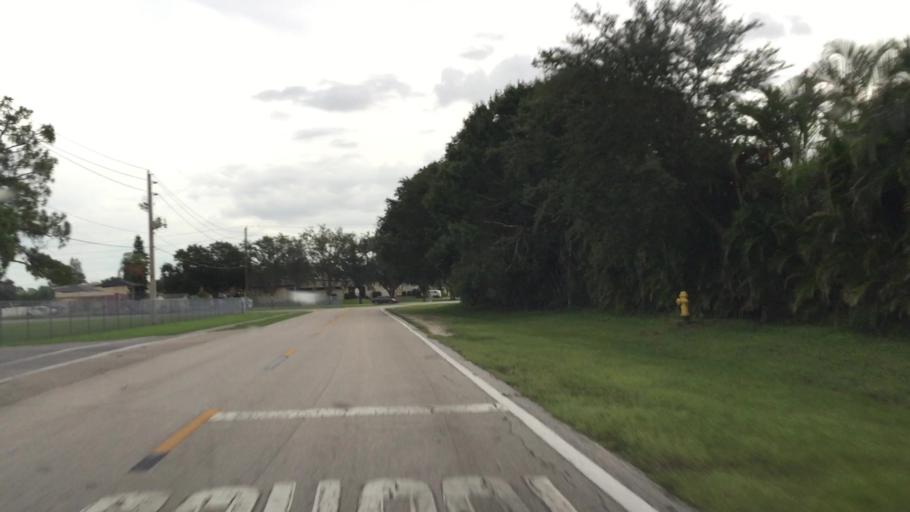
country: US
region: Florida
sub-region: Lee County
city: Pine Manor
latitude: 26.5677
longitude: -81.8689
